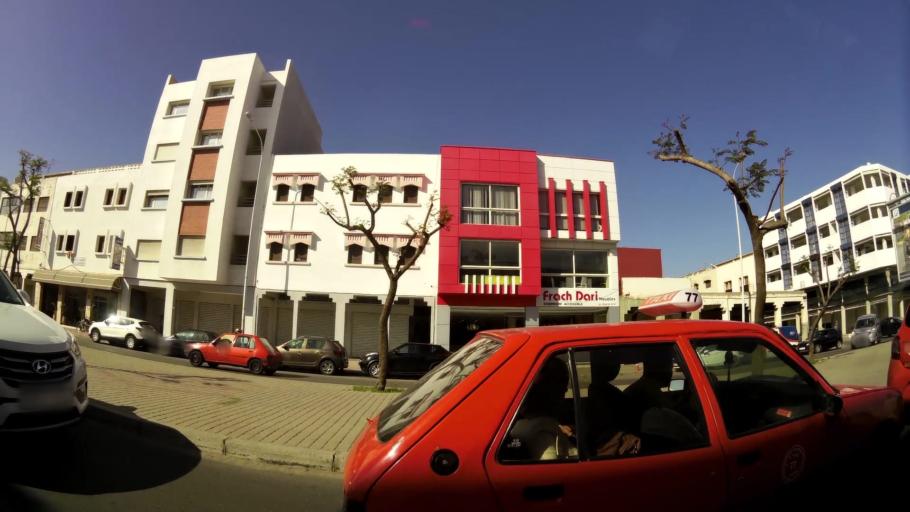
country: MA
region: Oued ed Dahab-Lagouira
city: Dakhla
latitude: 30.4089
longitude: -9.5579
